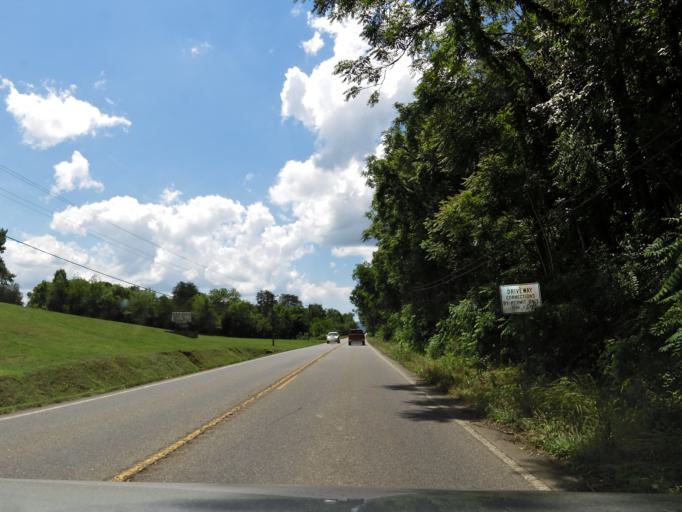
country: US
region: Tennessee
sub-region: Blount County
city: Maryville
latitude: 35.6937
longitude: -84.0425
